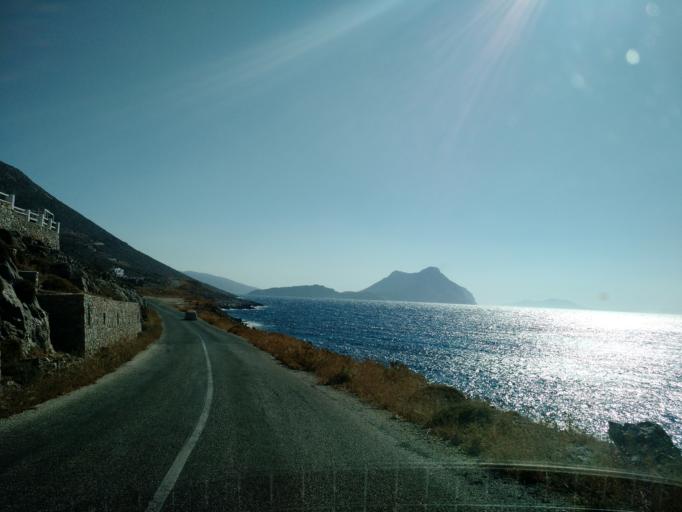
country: GR
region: South Aegean
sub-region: Nomos Kykladon
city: Amorgos
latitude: 36.8977
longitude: 25.9712
